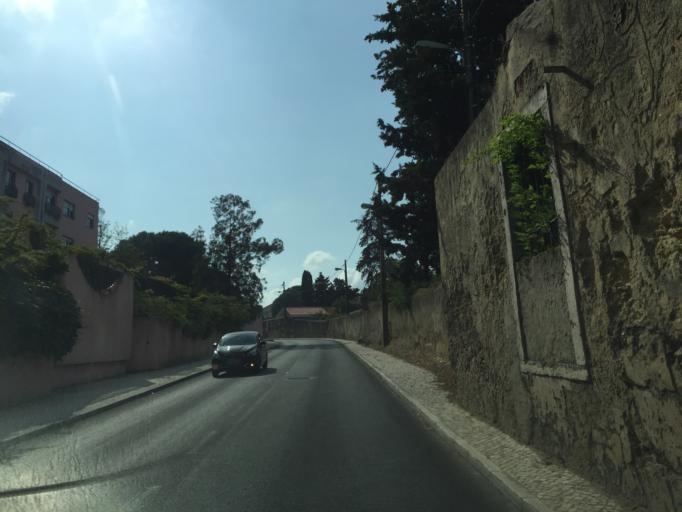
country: PT
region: Lisbon
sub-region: Odivelas
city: Olival do Basto
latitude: 38.7743
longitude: -9.1669
